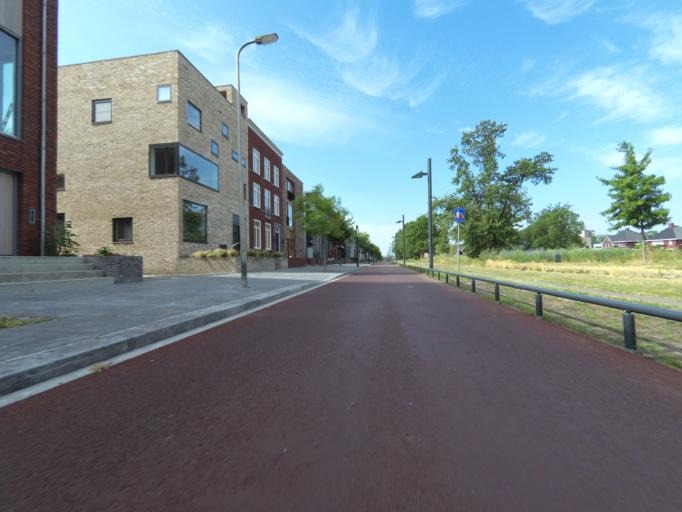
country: NL
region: Overijssel
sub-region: Gemeente Enschede
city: Enschede
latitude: 52.2367
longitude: 6.9000
